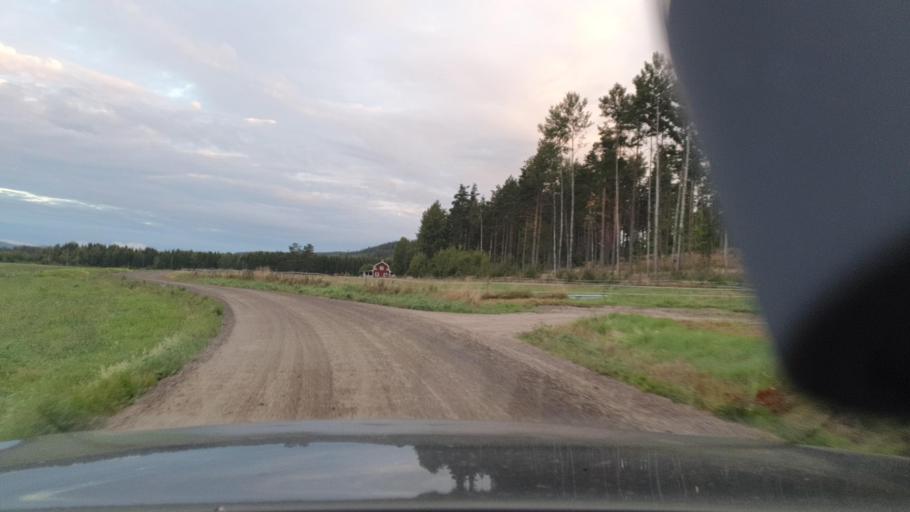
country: SE
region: Vaermland
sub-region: Sunne Kommun
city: Sunne
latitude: 59.8000
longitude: 13.1035
